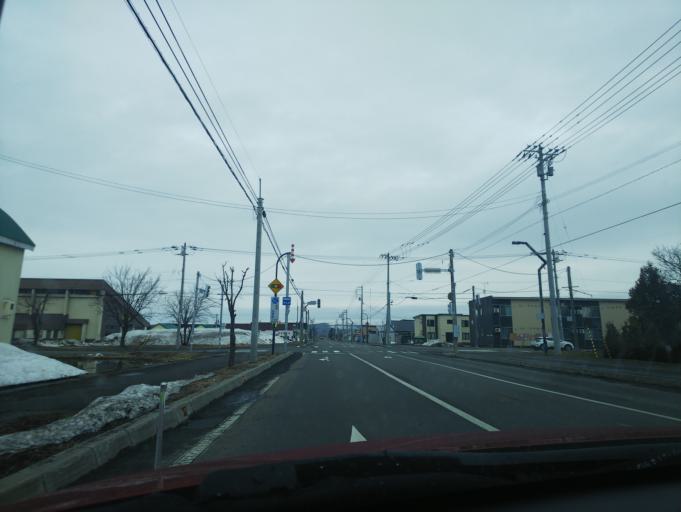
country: JP
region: Hokkaido
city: Nayoro
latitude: 44.3660
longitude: 142.4571
